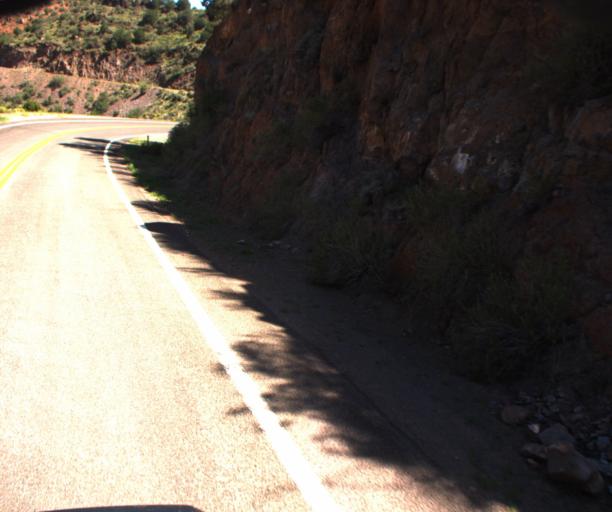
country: US
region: Arizona
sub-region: Greenlee County
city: Morenci
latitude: 33.1681
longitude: -109.3647
